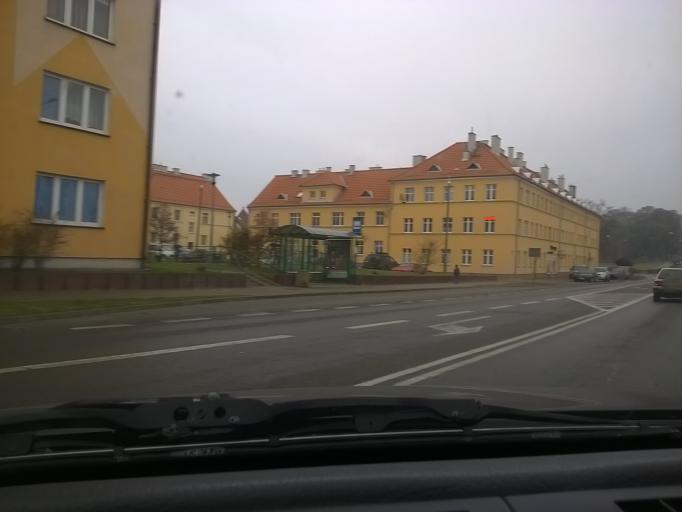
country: PL
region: Warmian-Masurian Voivodeship
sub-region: Powiat ketrzynski
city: Ketrzyn
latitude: 54.0811
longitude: 21.3609
